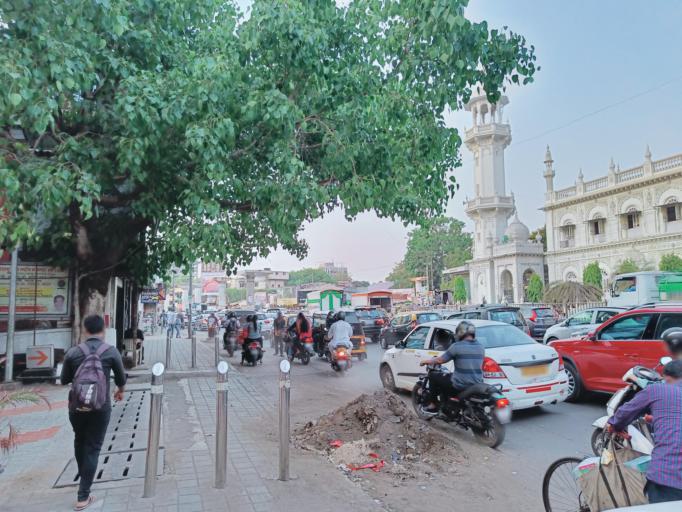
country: IN
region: Maharashtra
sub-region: Mumbai Suburban
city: Mumbai
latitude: 19.0514
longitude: 72.8382
